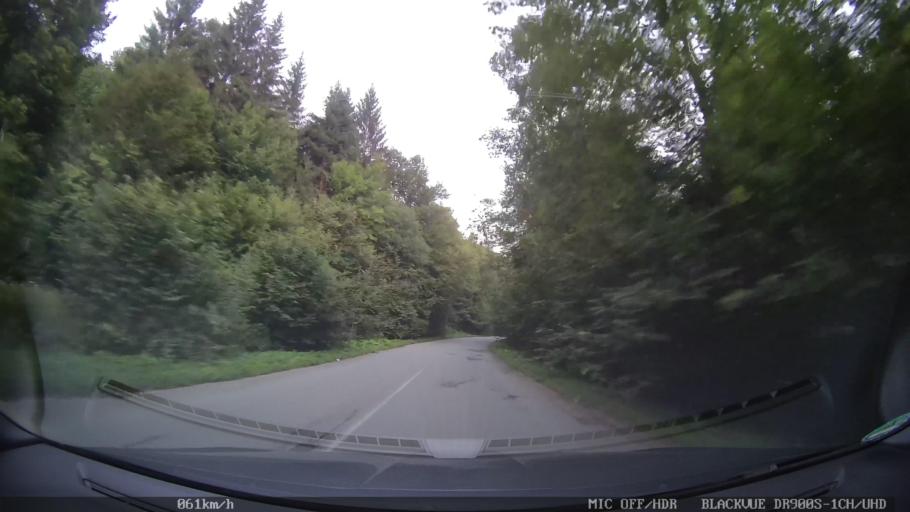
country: HR
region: Primorsko-Goranska
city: Vrbovsko
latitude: 45.2115
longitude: 15.0279
